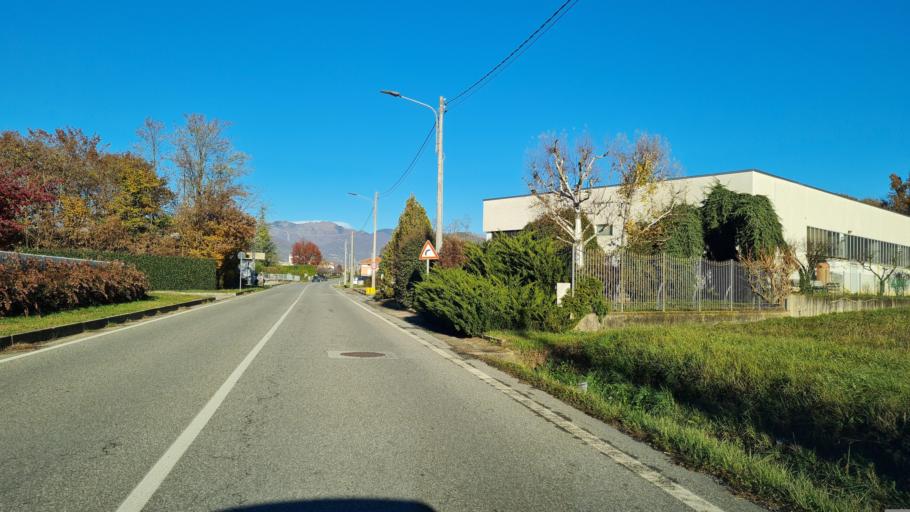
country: IT
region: Piedmont
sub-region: Provincia di Biella
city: Cossato
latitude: 45.5554
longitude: 8.2046
